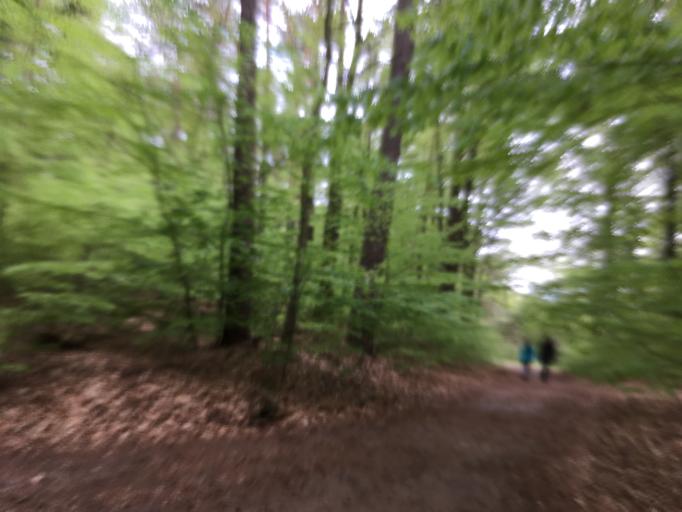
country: DE
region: Brandenburg
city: Rudnitz
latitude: 52.7331
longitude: 13.5975
